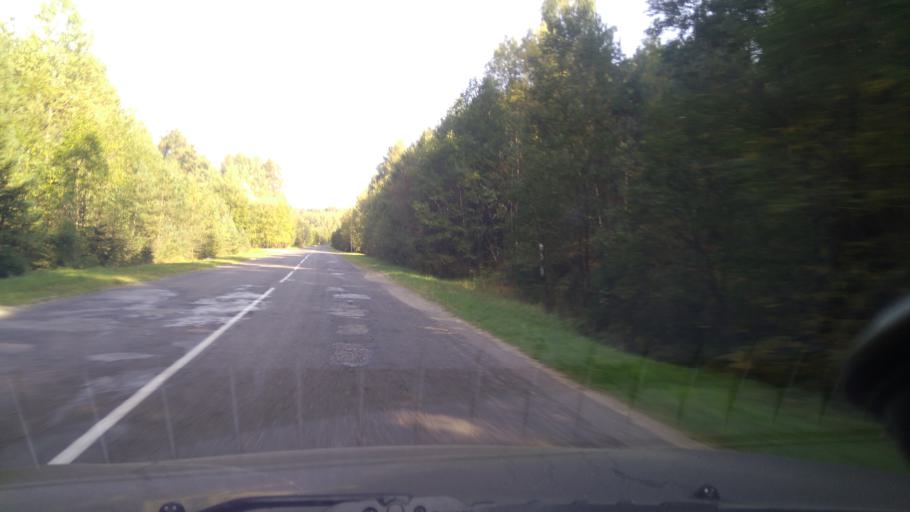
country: BY
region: Minsk
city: Rakaw
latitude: 53.9975
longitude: 27.0457
